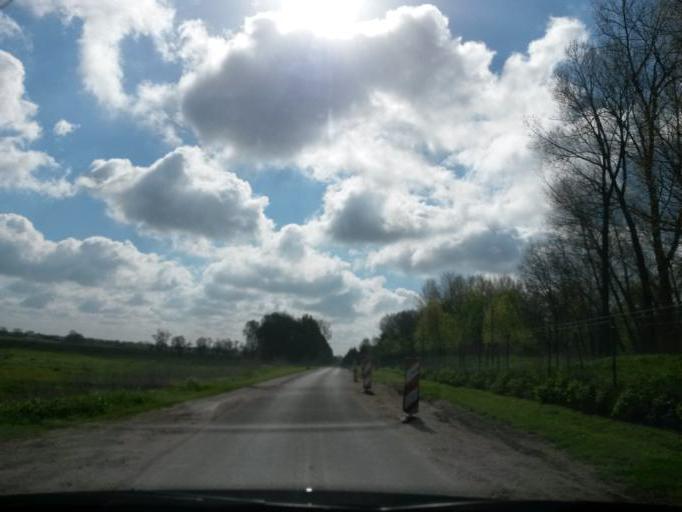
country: DE
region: Schleswig-Holstein
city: Haseldorf
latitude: 53.6075
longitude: 9.6146
